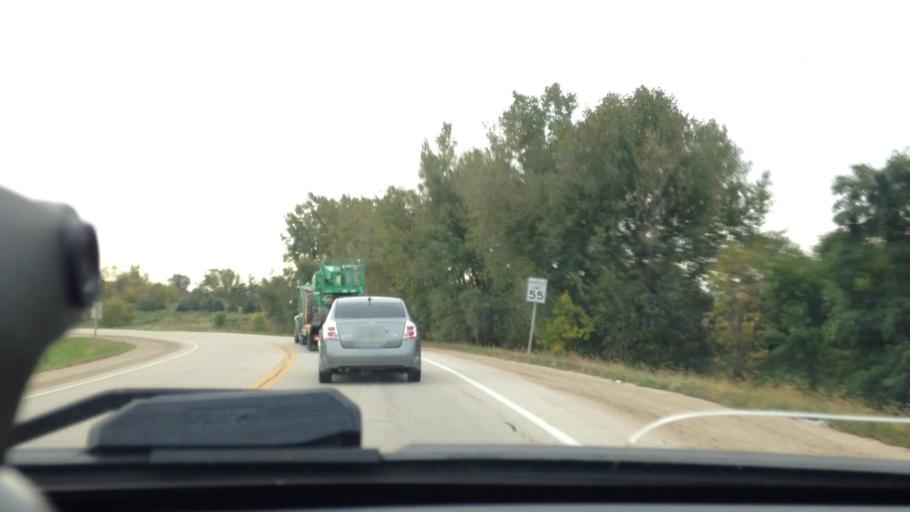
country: US
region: Wisconsin
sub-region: Fond du Lac County
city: North Fond du Lac
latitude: 43.8060
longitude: -88.5025
